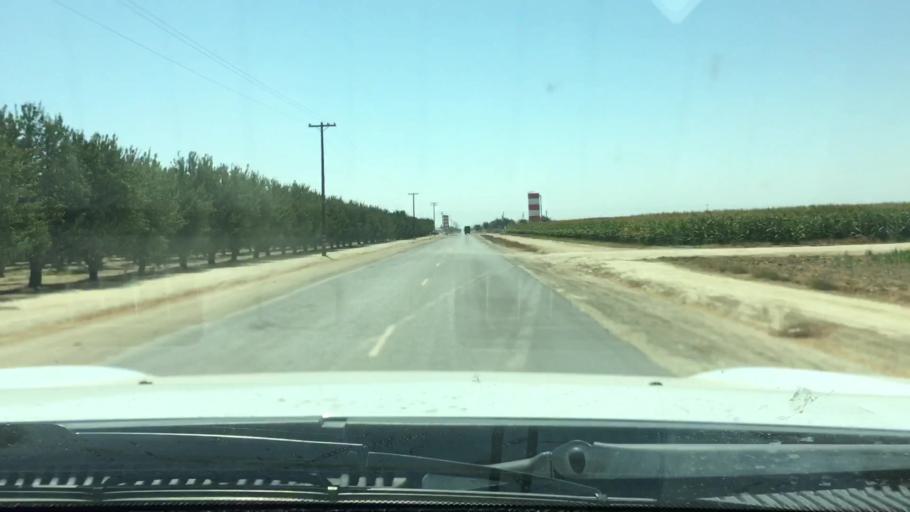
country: US
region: California
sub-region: Kern County
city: Wasco
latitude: 35.5685
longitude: -119.4028
